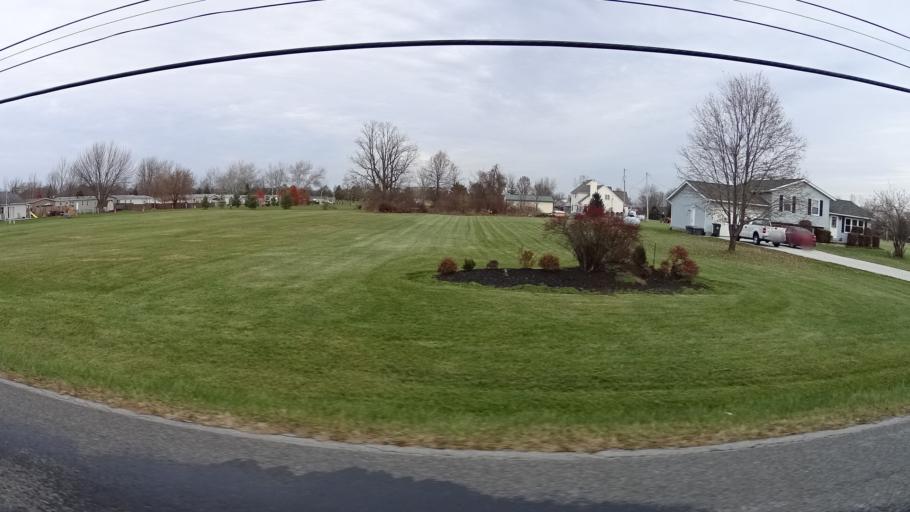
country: US
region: Ohio
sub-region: Lorain County
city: Lagrange
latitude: 41.1998
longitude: -82.1412
